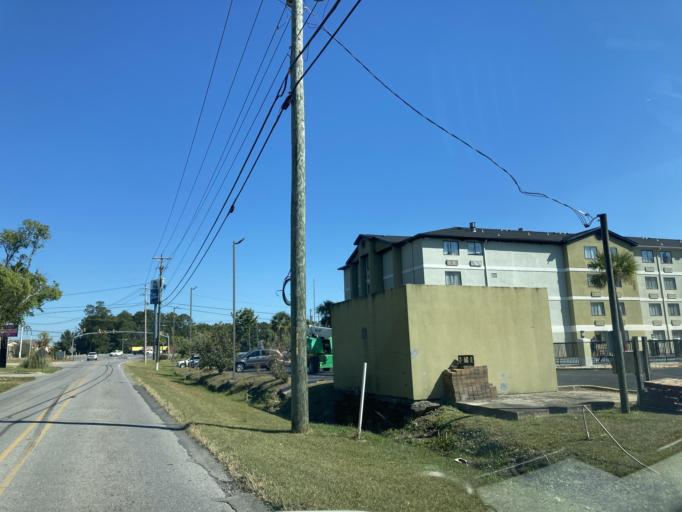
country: US
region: Mississippi
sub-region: Jackson County
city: Gulf Hills
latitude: 30.4576
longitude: -88.8454
